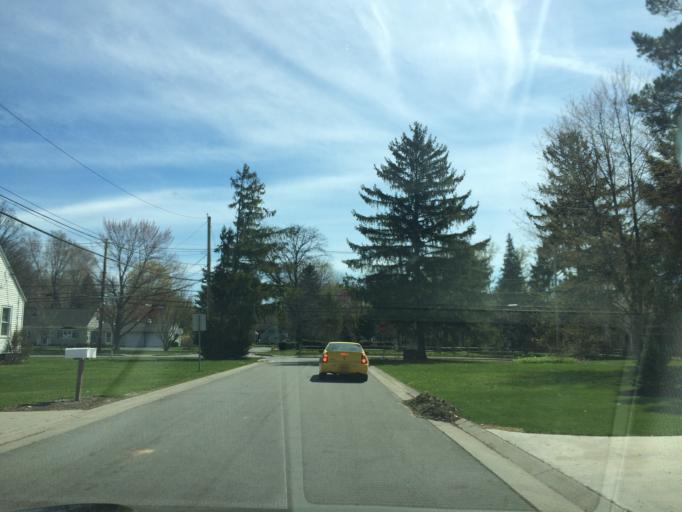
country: US
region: New York
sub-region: Monroe County
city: Fairport
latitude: 43.0897
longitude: -77.4630
